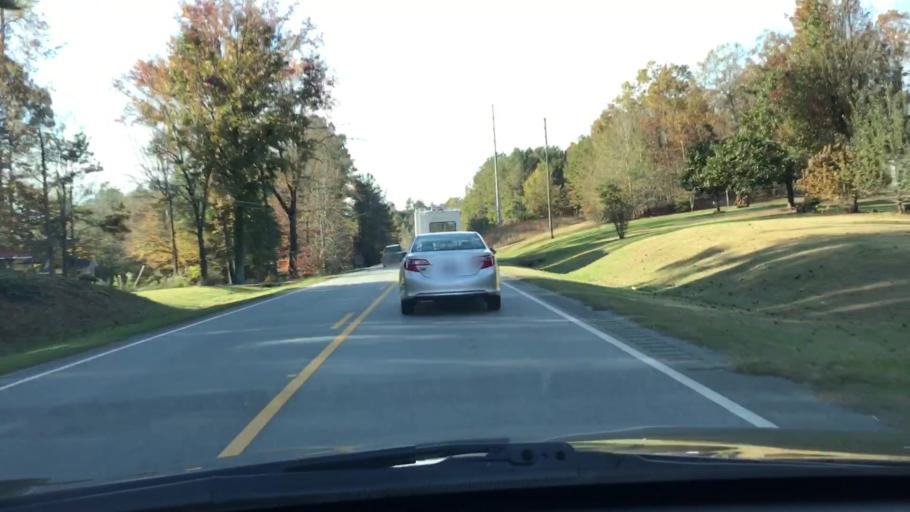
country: US
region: Alabama
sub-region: Cleburne County
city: Heflin
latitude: 33.6534
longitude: -85.5248
